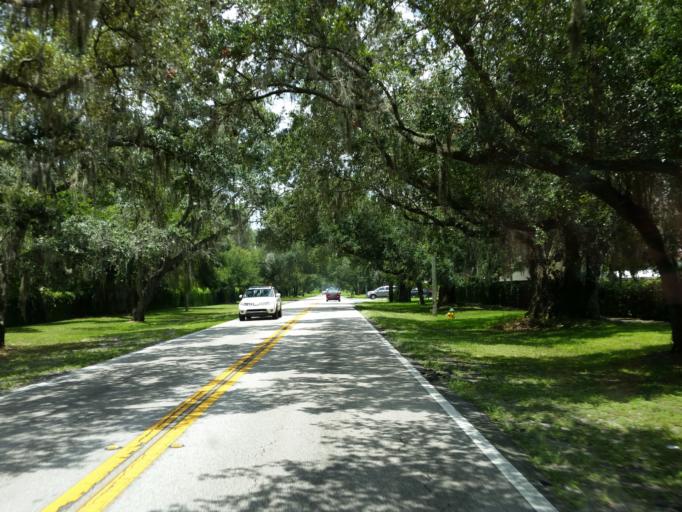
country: US
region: Florida
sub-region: Hillsborough County
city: Bloomingdale
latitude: 27.8691
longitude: -82.2692
